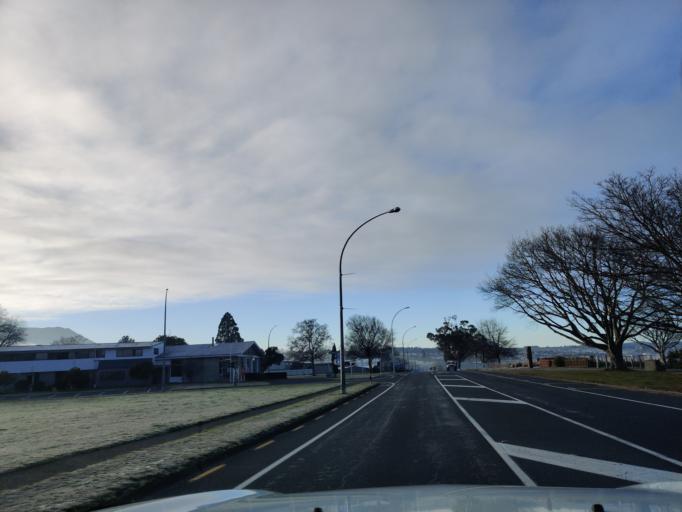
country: NZ
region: Waikato
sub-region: Taupo District
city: Taupo
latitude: -38.6928
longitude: 176.0751
